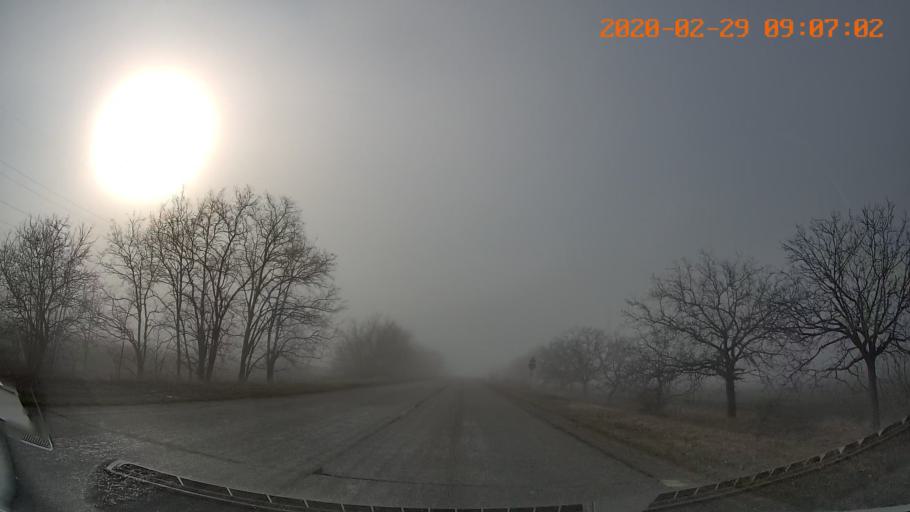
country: MD
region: Telenesti
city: Tiraspolul Nou
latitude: 46.8676
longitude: 29.7471
